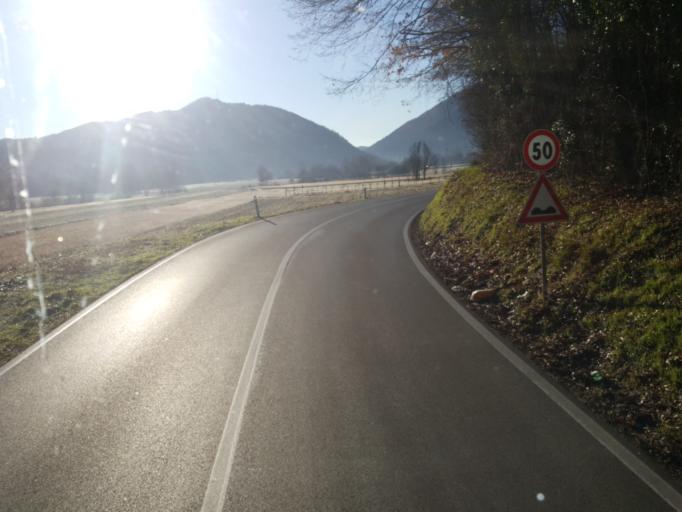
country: IT
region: Latium
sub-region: Provincia di Rieti
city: Colli sul Velino
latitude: 42.5151
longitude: 12.7382
